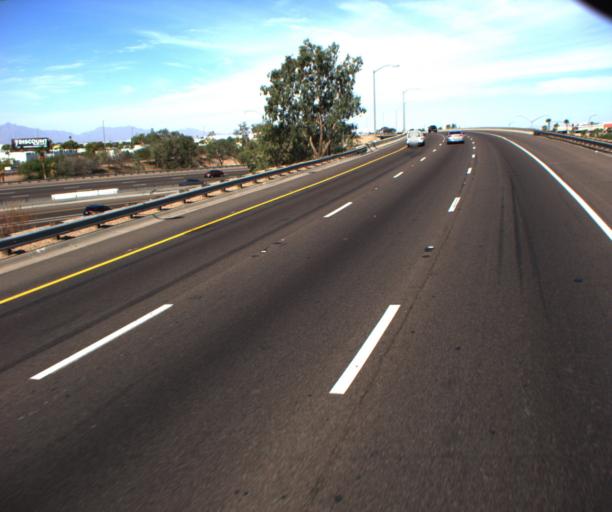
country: US
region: Arizona
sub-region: Maricopa County
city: Phoenix
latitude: 33.4278
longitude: -112.0344
